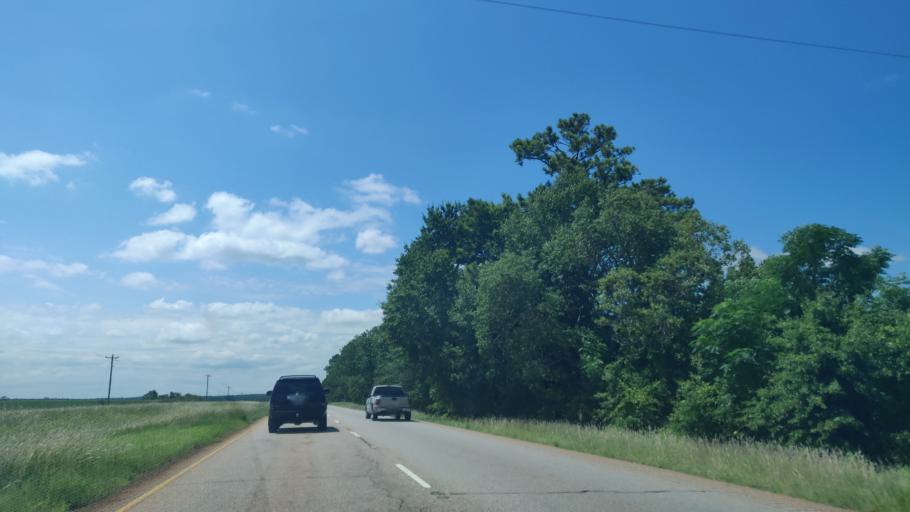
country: US
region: Georgia
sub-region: Stewart County
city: Richland
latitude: 32.0645
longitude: -84.6717
